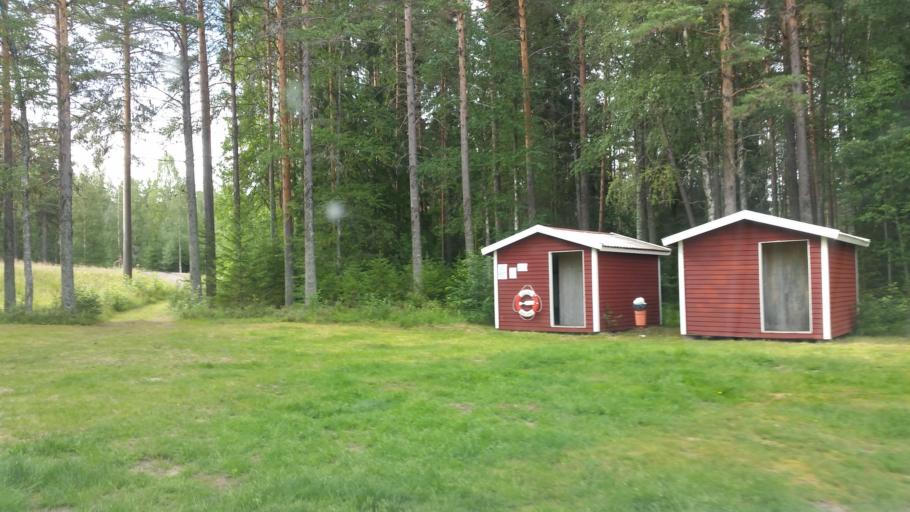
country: SE
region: Vaesternorrland
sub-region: Ange Kommun
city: Ange
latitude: 62.1915
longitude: 15.6609
